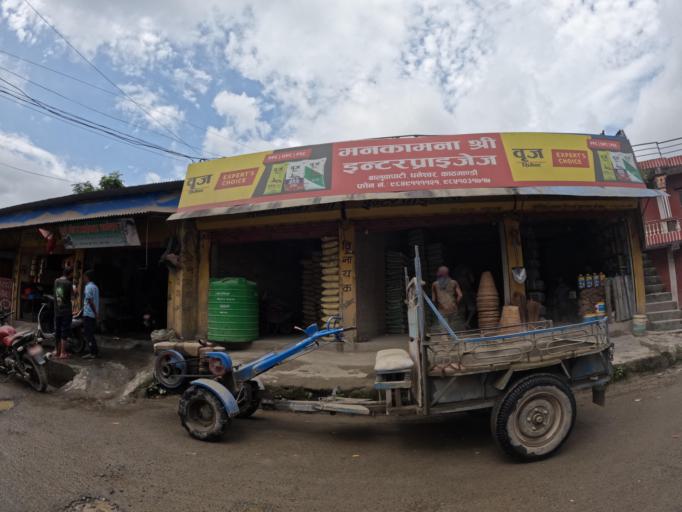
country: NP
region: Central Region
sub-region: Bagmati Zone
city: Kathmandu
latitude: 27.7519
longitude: 85.3176
